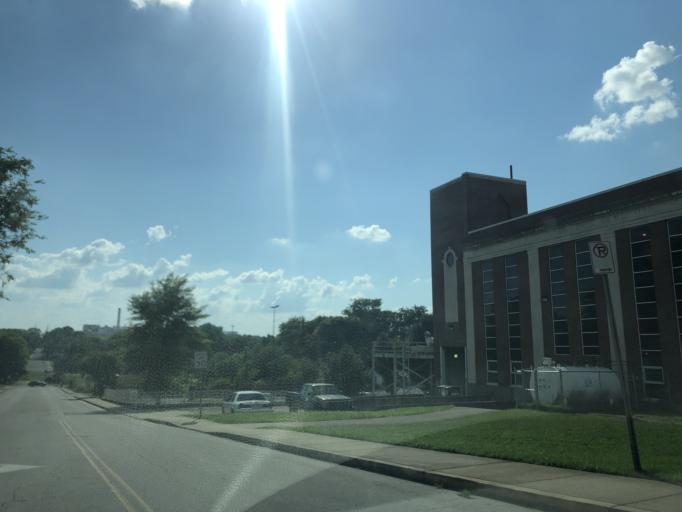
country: US
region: Tennessee
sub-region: Davidson County
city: Nashville
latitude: 36.1662
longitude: -86.8321
